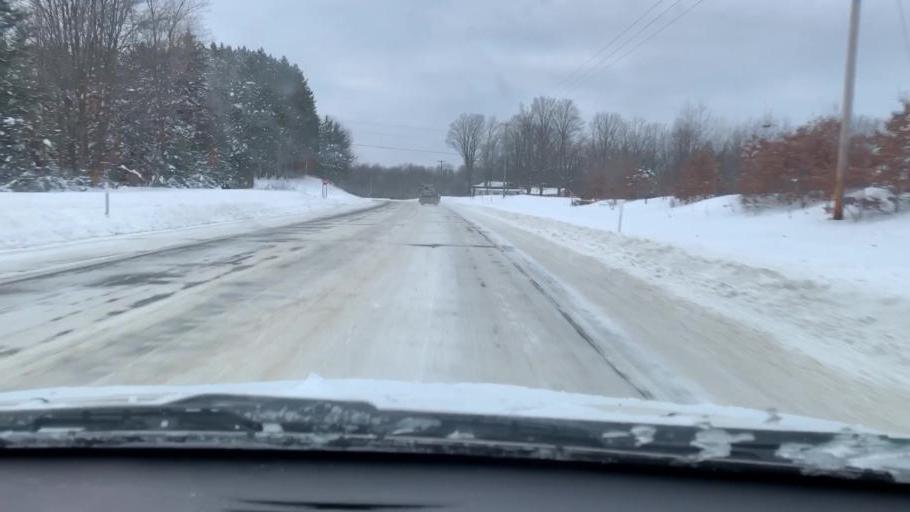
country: US
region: Michigan
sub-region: Wexford County
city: Manton
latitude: 44.5849
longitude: -85.3558
